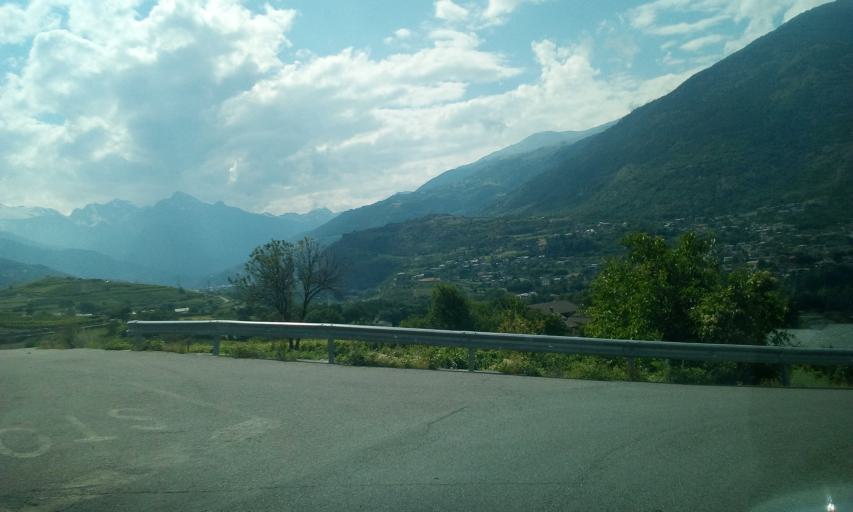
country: IT
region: Aosta Valley
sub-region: Valle d'Aosta
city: Jovencan
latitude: 45.7107
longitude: 7.2719
